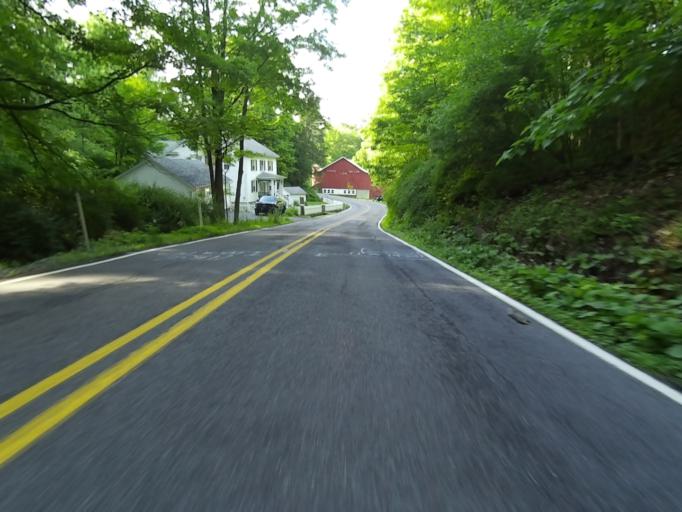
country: US
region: Pennsylvania
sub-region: Centre County
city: Park Forest Village
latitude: 40.8117
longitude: -77.9538
